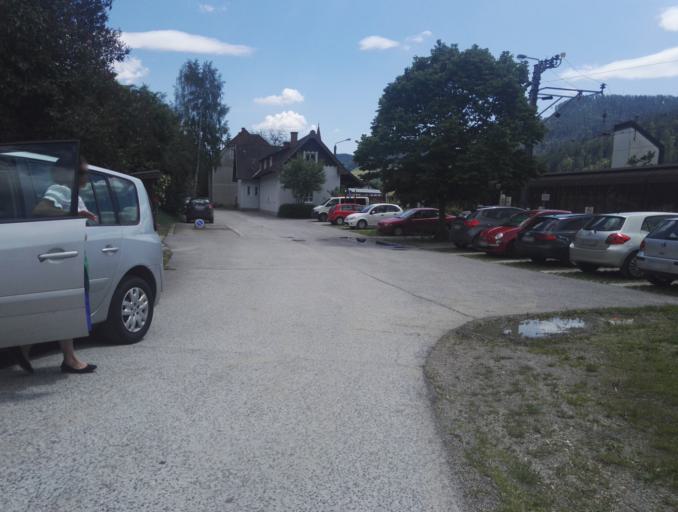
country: AT
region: Styria
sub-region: Politischer Bezirk Graz-Umgebung
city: Ubelbach
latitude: 47.2251
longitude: 15.2367
